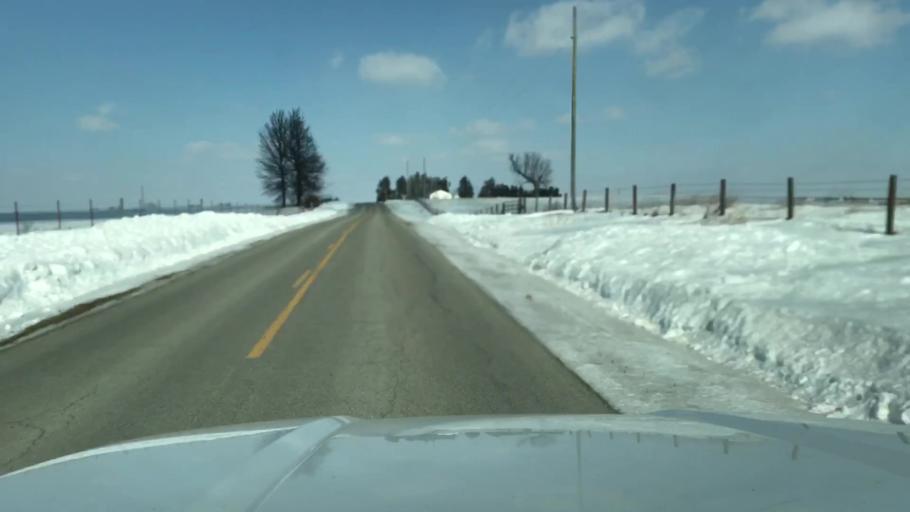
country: US
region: Missouri
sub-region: Nodaway County
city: Maryville
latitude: 40.3704
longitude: -94.7215
